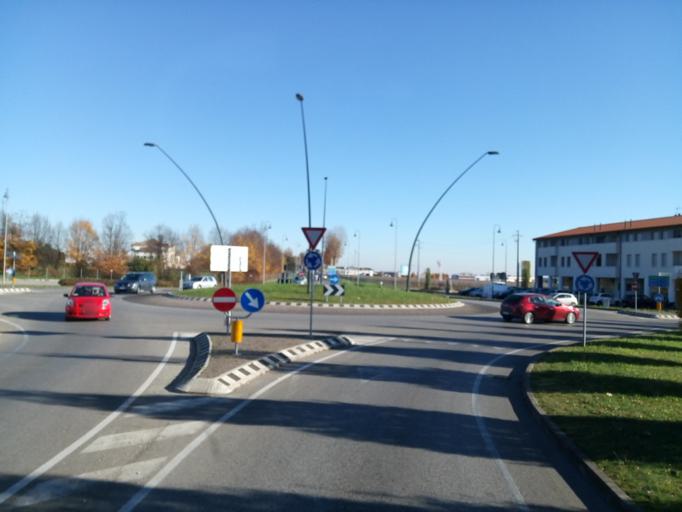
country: IT
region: Veneto
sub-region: Provincia di Treviso
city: Venegazzu
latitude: 45.7770
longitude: 12.0944
